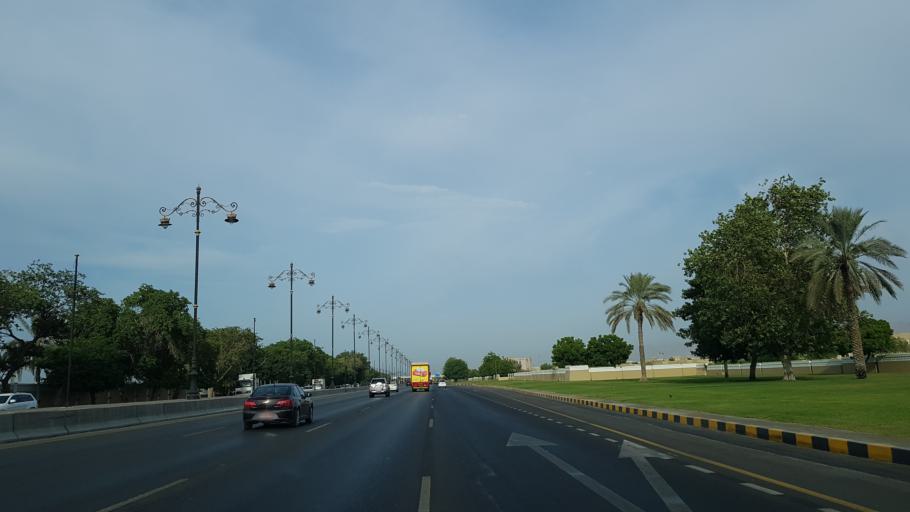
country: OM
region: Muhafazat Masqat
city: Bawshar
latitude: 23.5847
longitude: 58.2822
